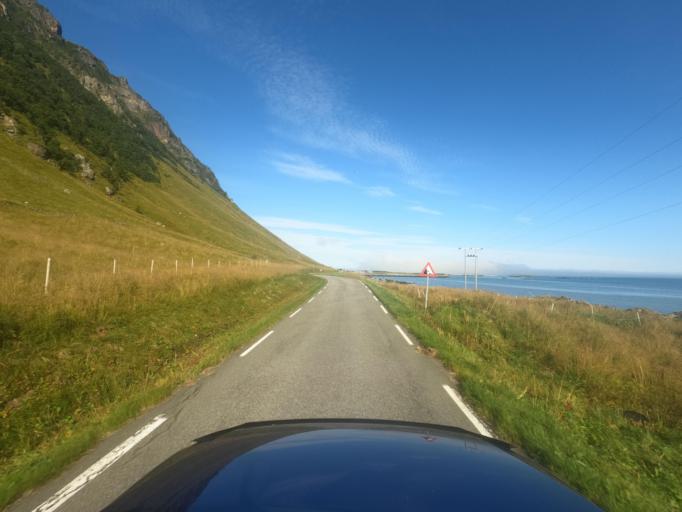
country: NO
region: Nordland
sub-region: Vestvagoy
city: Evjen
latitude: 68.3270
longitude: 14.0004
